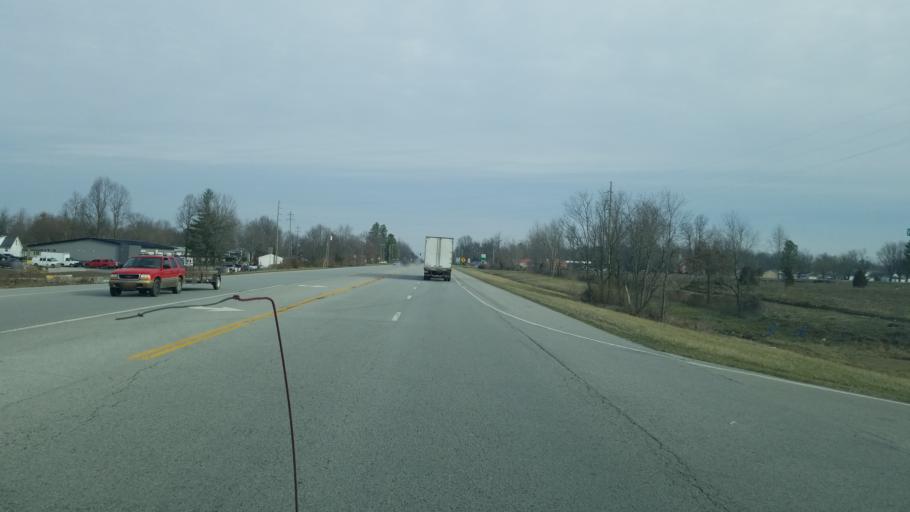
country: US
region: Kentucky
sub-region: Boyle County
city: Junction City
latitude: 37.5795
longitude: -84.7891
